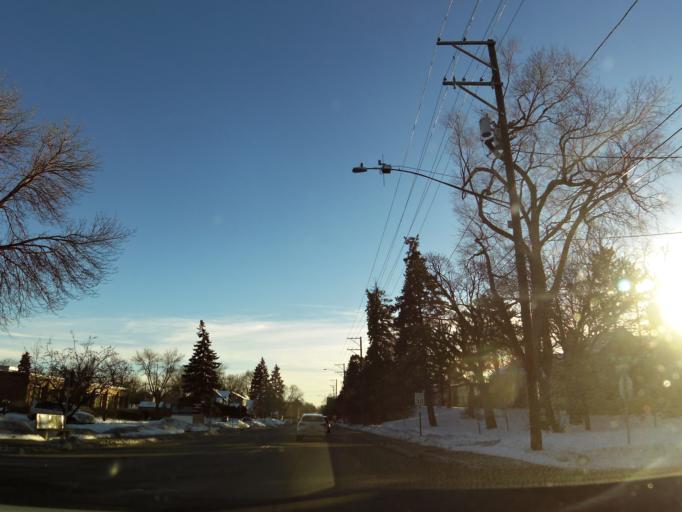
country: US
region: Minnesota
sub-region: Hennepin County
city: Edina
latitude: 44.9162
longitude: -93.3292
